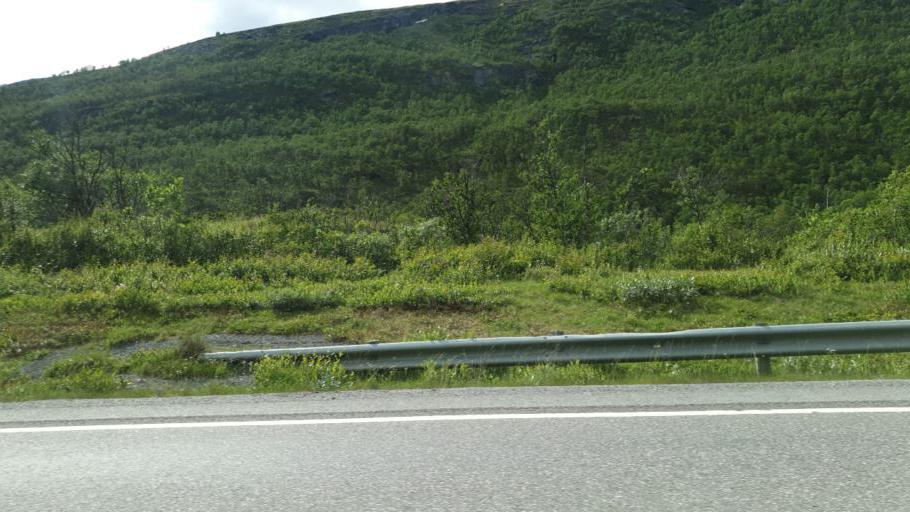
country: NO
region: Sor-Trondelag
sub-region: Oppdal
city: Oppdal
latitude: 62.3220
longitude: 9.6206
